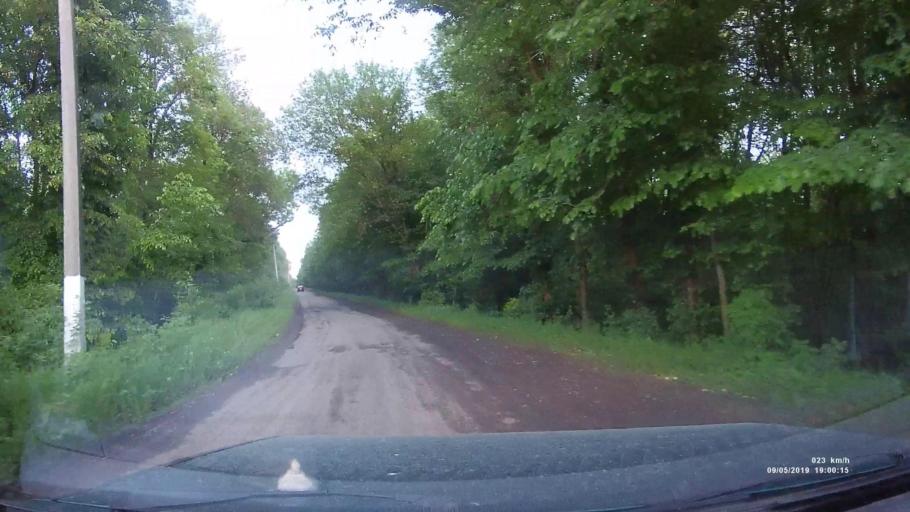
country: RU
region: Krasnodarskiy
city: Kanelovskaya
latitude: 46.7524
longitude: 39.1350
